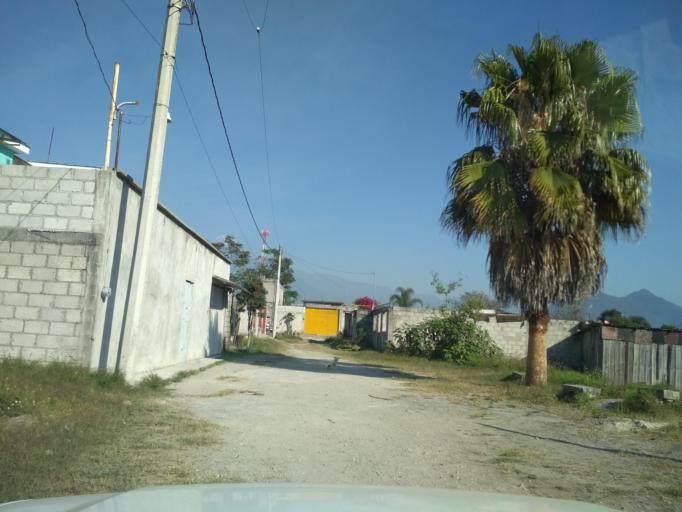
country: MX
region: Veracruz
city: Jalapilla
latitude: 18.8212
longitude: -97.0818
